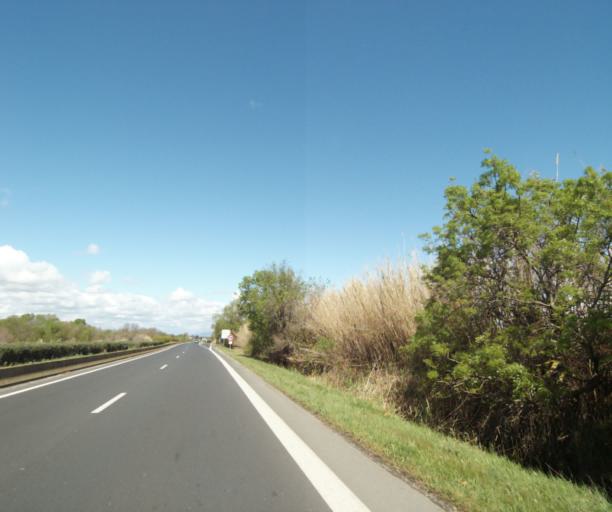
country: FR
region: Languedoc-Roussillon
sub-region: Departement de l'Herault
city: Lattes
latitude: 43.5458
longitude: 3.8956
